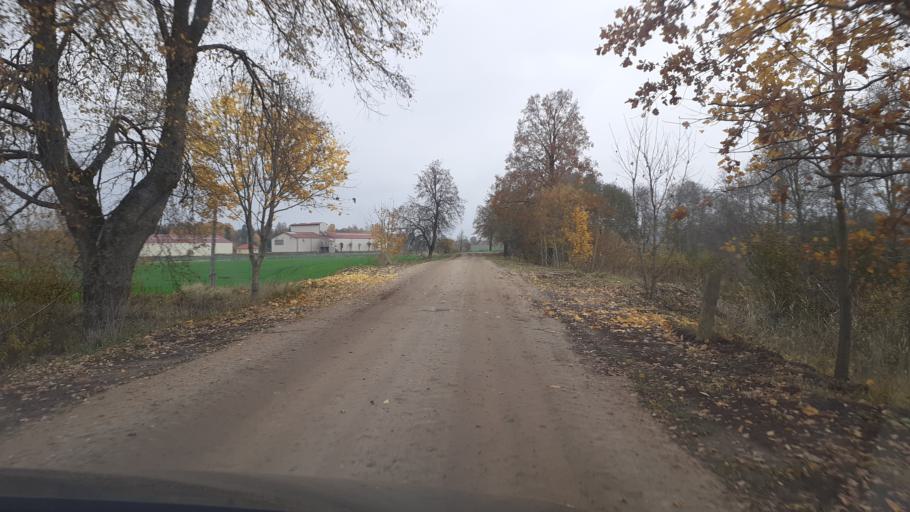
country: LV
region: Skrunda
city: Skrunda
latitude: 56.8510
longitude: 22.2141
